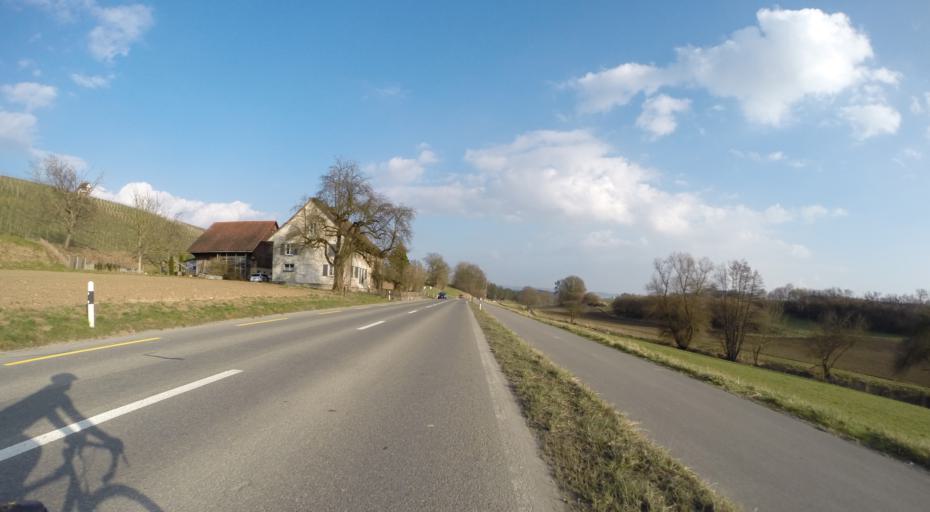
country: CH
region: Thurgau
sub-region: Frauenfeld District
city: Huttwilen
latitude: 47.6051
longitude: 8.8729
